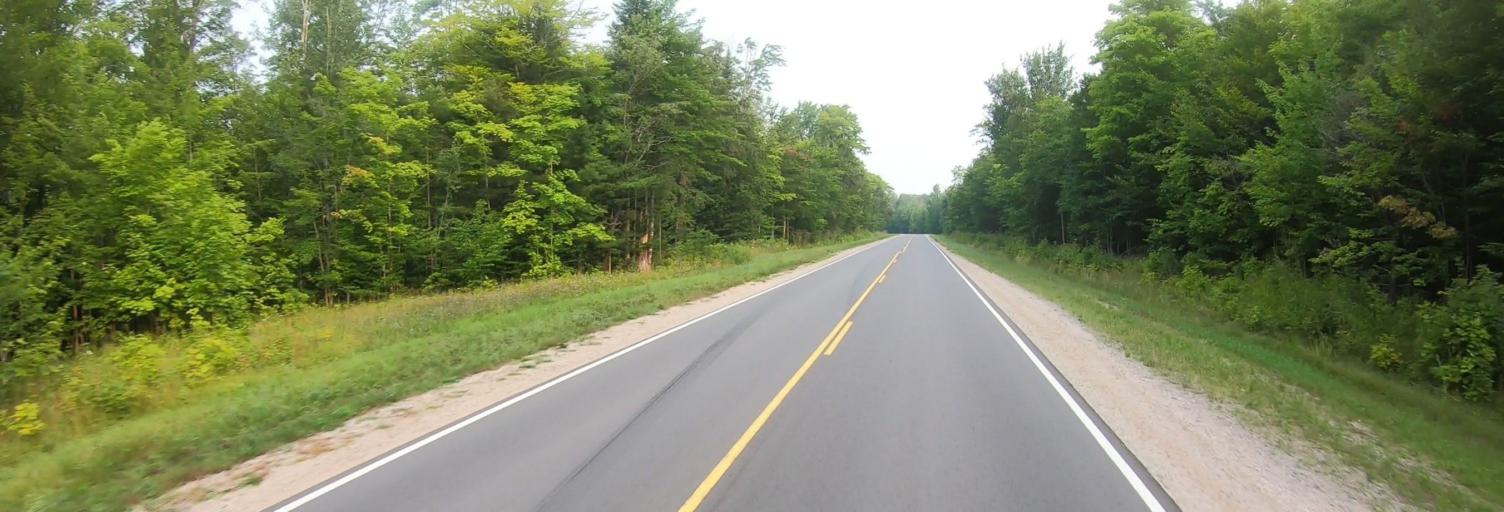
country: US
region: Michigan
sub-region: Luce County
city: Newberry
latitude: 46.4832
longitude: -85.0806
